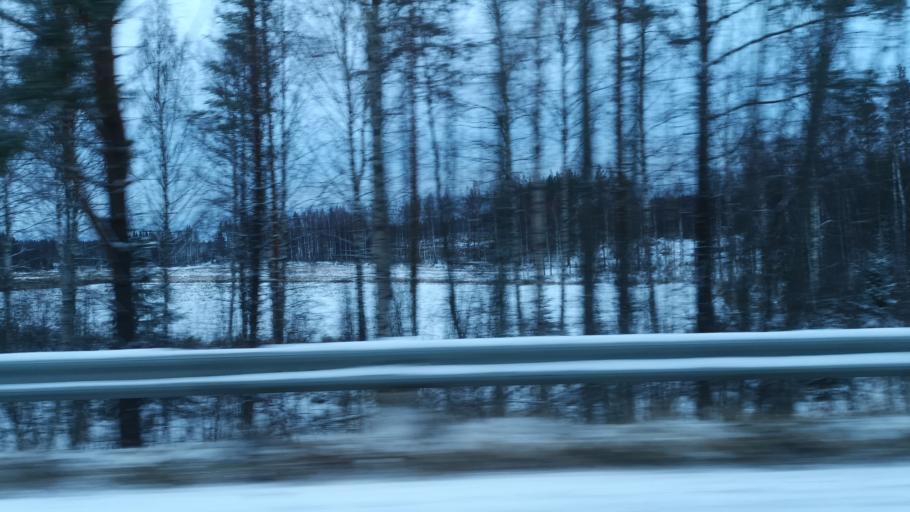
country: FI
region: Southern Savonia
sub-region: Savonlinna
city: Enonkoski
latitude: 62.1087
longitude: 28.6218
